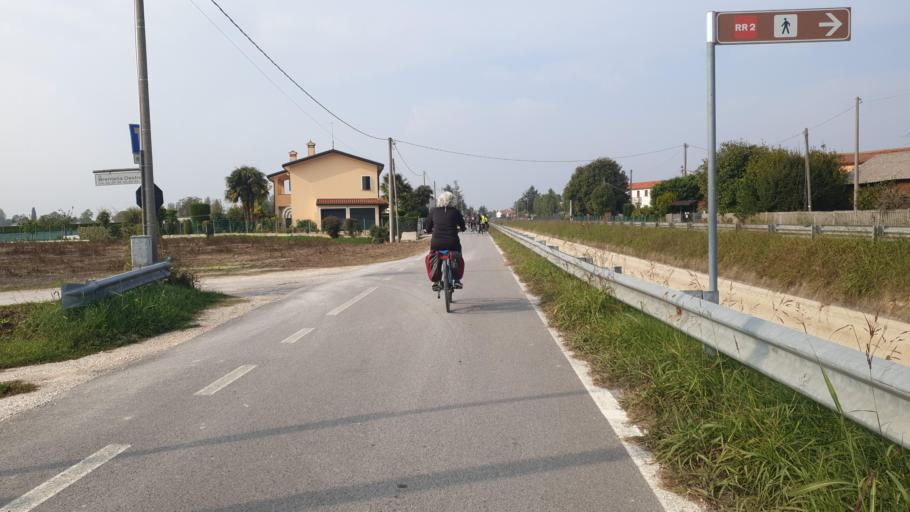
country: IT
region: Veneto
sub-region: Provincia di Padova
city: Corte
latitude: 45.3042
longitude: 12.0757
